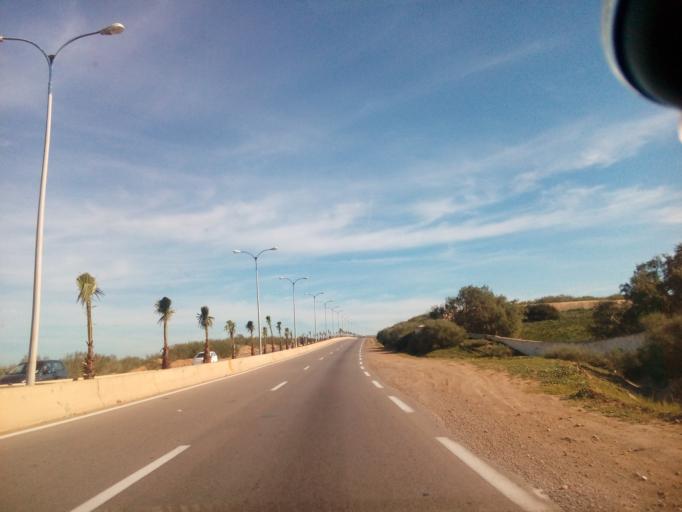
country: DZ
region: Mostaganem
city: Mostaganem
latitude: 35.8357
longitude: -0.0064
